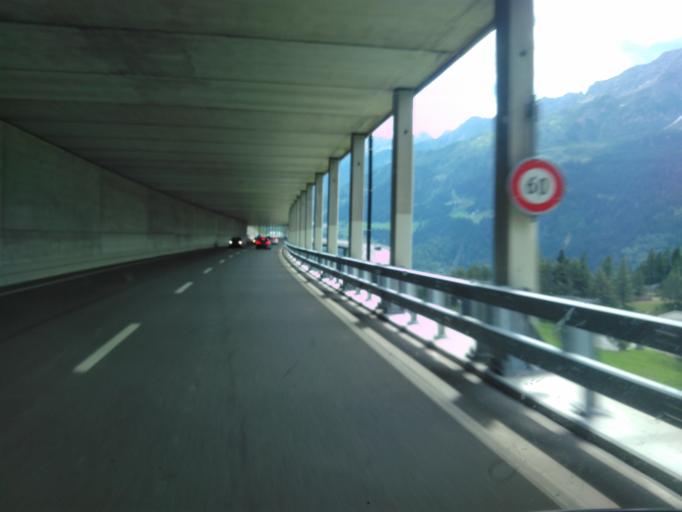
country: CH
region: Ticino
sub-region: Leventina District
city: Airolo
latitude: 46.5364
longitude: 8.5880
